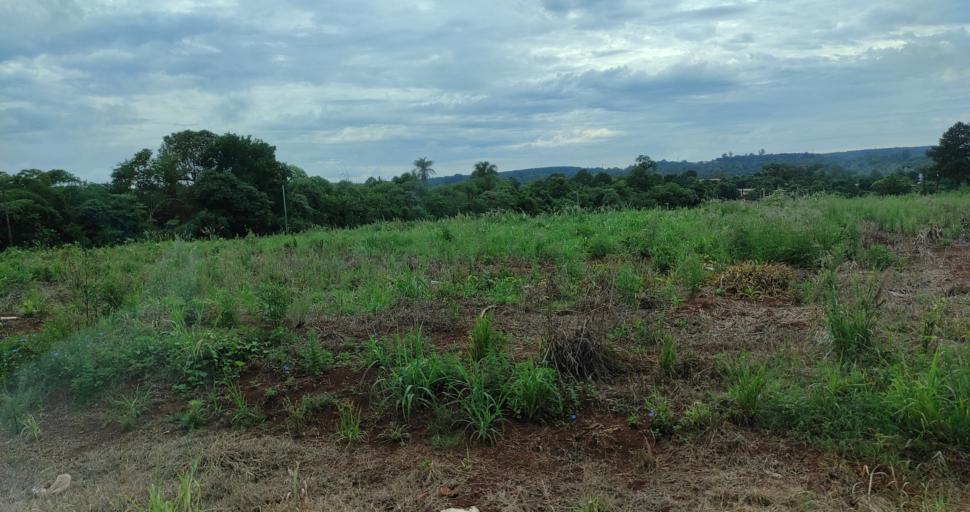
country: AR
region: Misiones
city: Puerto Libertad
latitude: -25.9650
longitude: -54.5938
